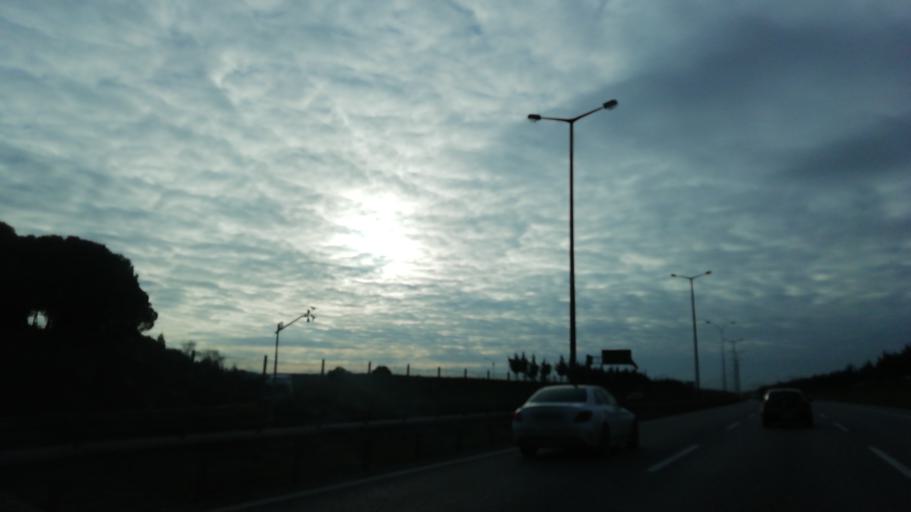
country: TR
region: Istanbul
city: Icmeler
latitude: 40.9213
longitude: 29.3513
